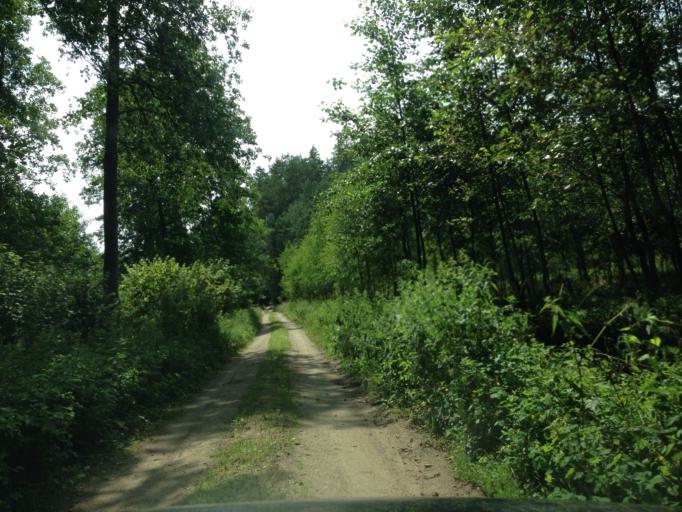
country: PL
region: Kujawsko-Pomorskie
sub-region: Powiat brodnicki
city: Bartniczka
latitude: 53.2774
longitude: 19.5728
